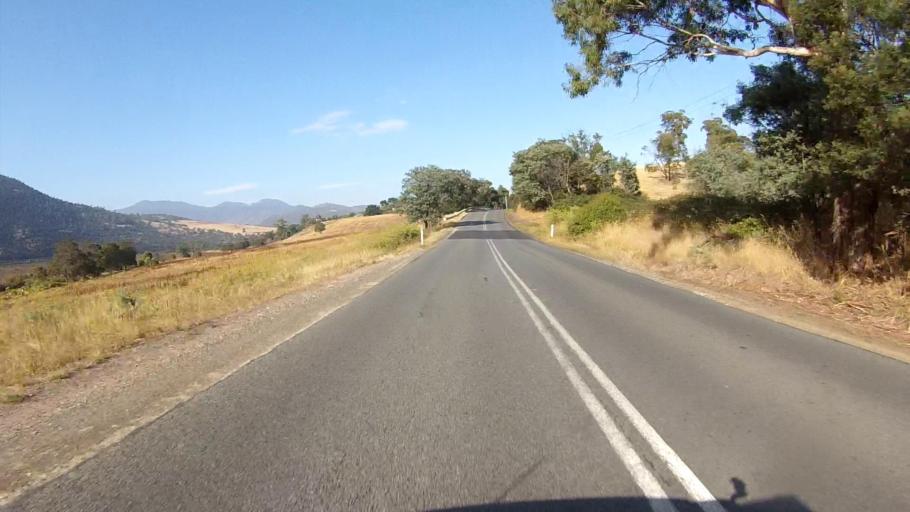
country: AU
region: Tasmania
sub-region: Derwent Valley
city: New Norfolk
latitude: -42.7600
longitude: 147.1377
